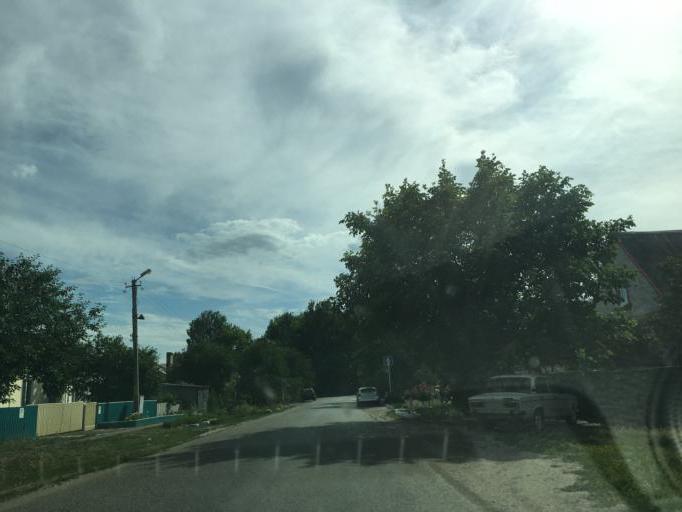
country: RU
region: Krasnodarskiy
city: Kushchevskaya
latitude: 46.5498
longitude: 39.6187
